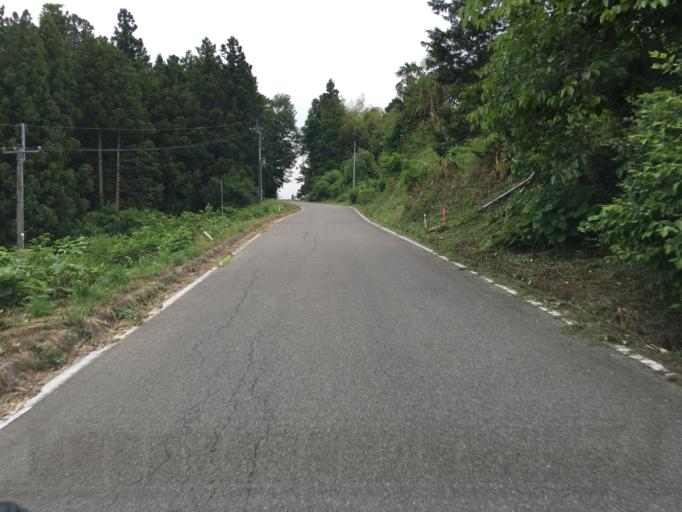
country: JP
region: Fukushima
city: Nihommatsu
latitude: 37.6240
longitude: 140.5275
